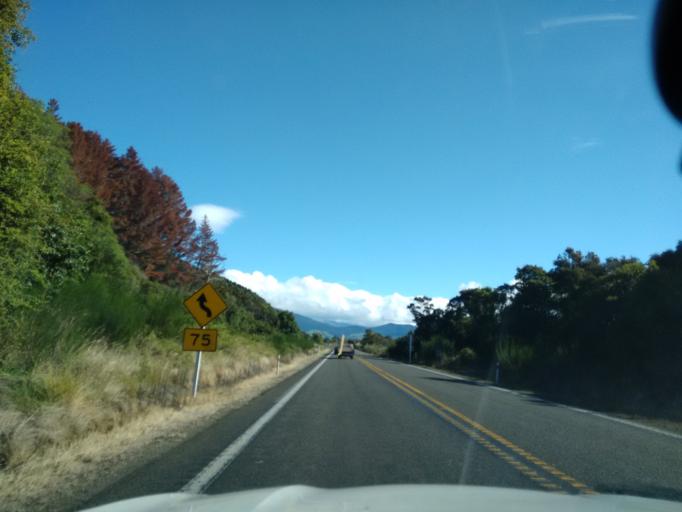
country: NZ
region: Waikato
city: Turangi
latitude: -38.9383
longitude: 175.8603
